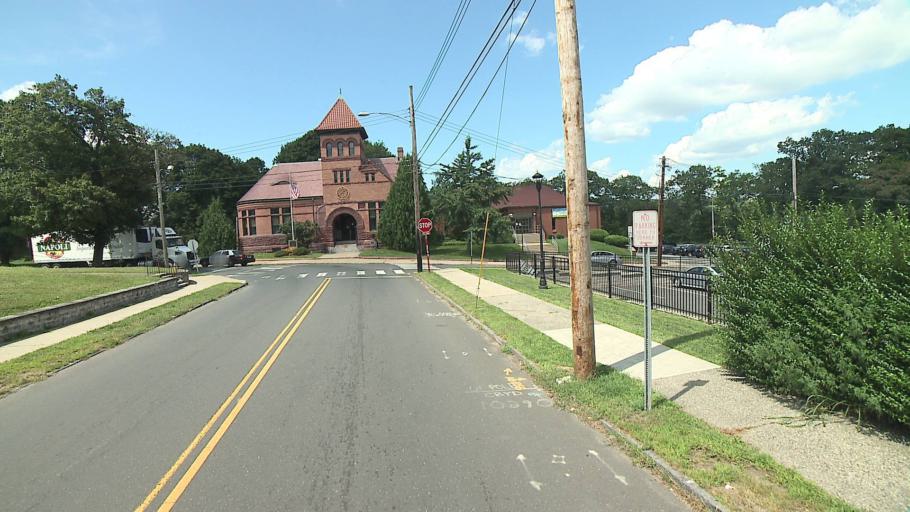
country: US
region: Connecticut
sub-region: Fairfield County
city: Shelton
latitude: 41.3192
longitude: -73.0977
